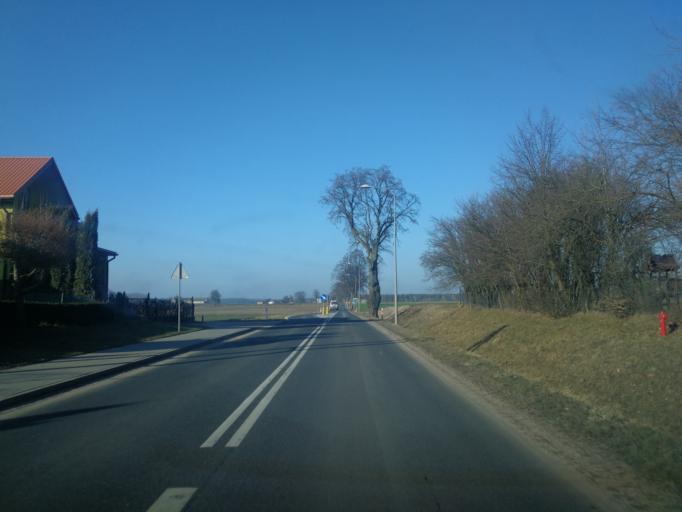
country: PL
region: Warmian-Masurian Voivodeship
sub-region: Powiat dzialdowski
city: Lidzbark
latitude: 53.3494
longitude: 19.8225
